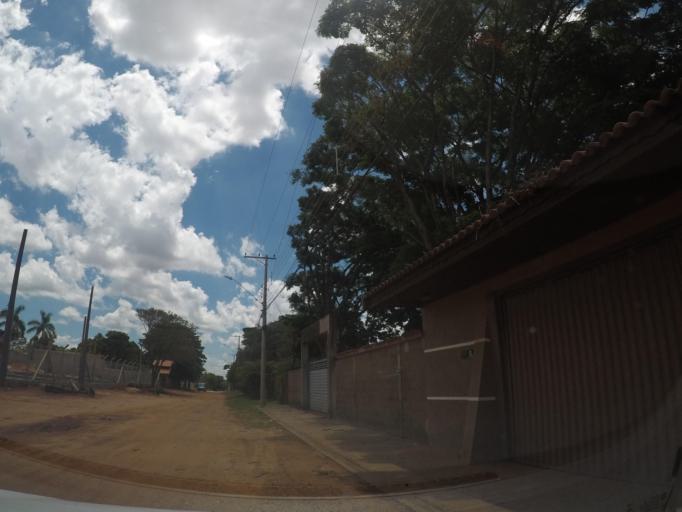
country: BR
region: Sao Paulo
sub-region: Hortolandia
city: Hortolandia
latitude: -22.8404
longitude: -47.2333
